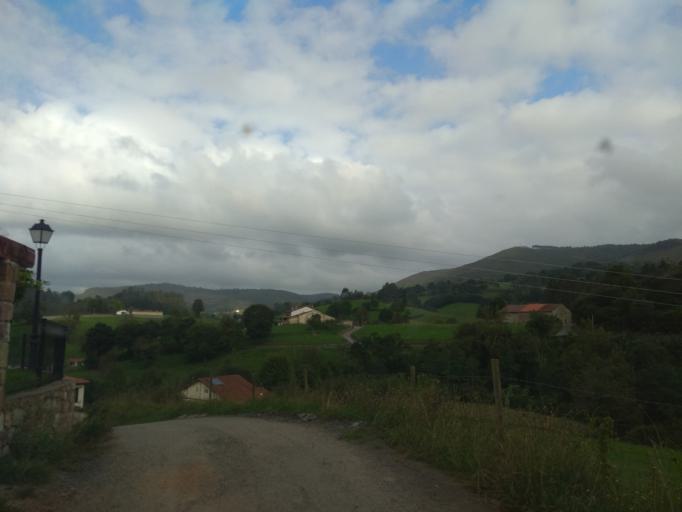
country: ES
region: Cantabria
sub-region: Provincia de Cantabria
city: San Vicente de la Barquera
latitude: 43.3177
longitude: -4.3532
